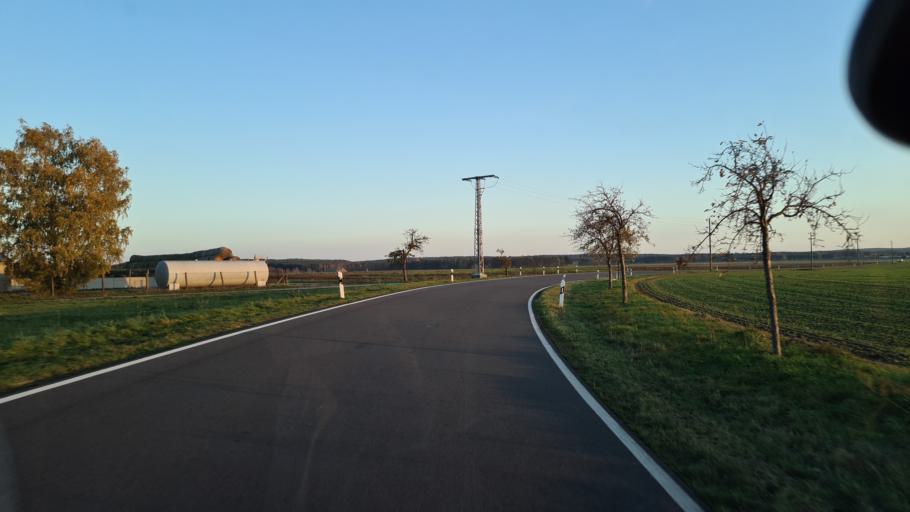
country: DE
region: Saxony
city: Torgau
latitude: 51.4917
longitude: 13.0015
